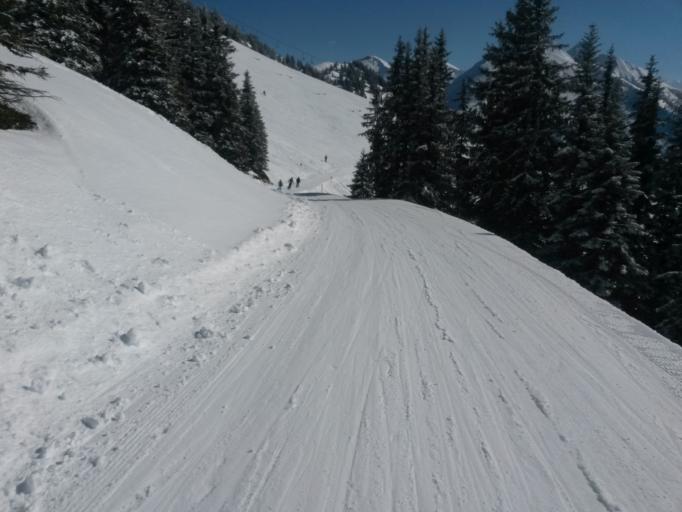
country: AT
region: Salzburg
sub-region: Politischer Bezirk Sankt Johann im Pongau
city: Dorfgastein
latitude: 47.2282
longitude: 13.1493
